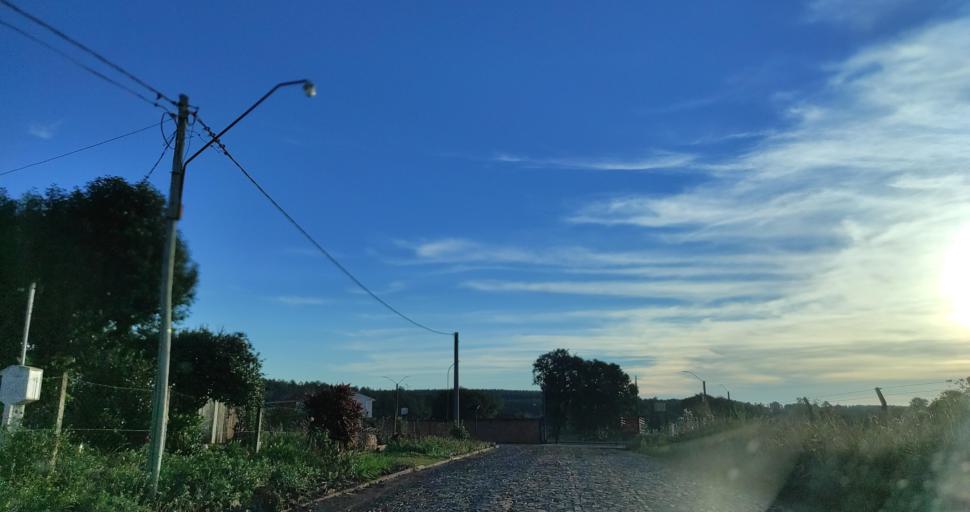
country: AR
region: Misiones
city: Capiovi
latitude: -26.8632
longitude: -55.0469
